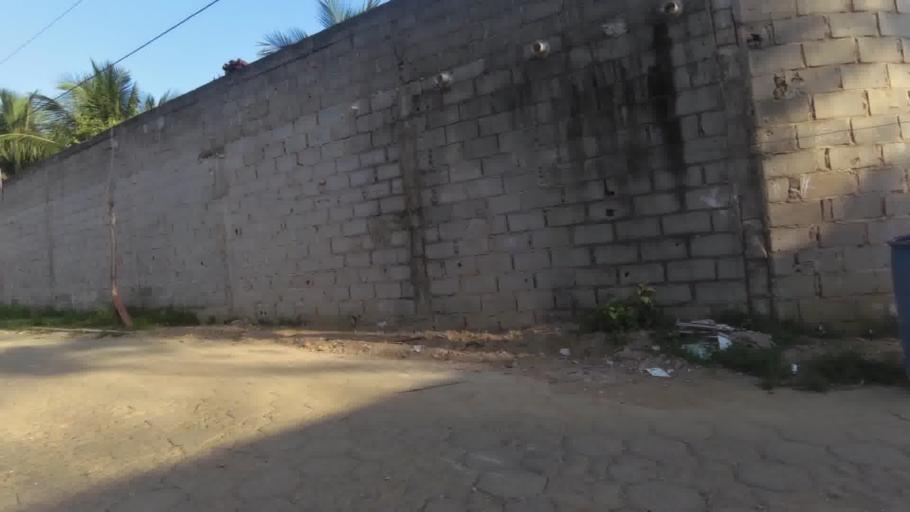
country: BR
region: Espirito Santo
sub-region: Piuma
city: Piuma
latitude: -20.8227
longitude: -40.7198
